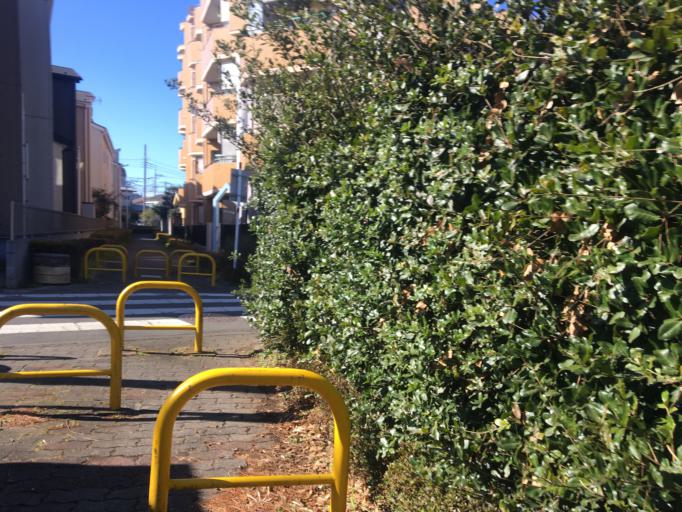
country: JP
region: Saitama
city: Shiki
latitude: 35.8109
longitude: 139.5722
